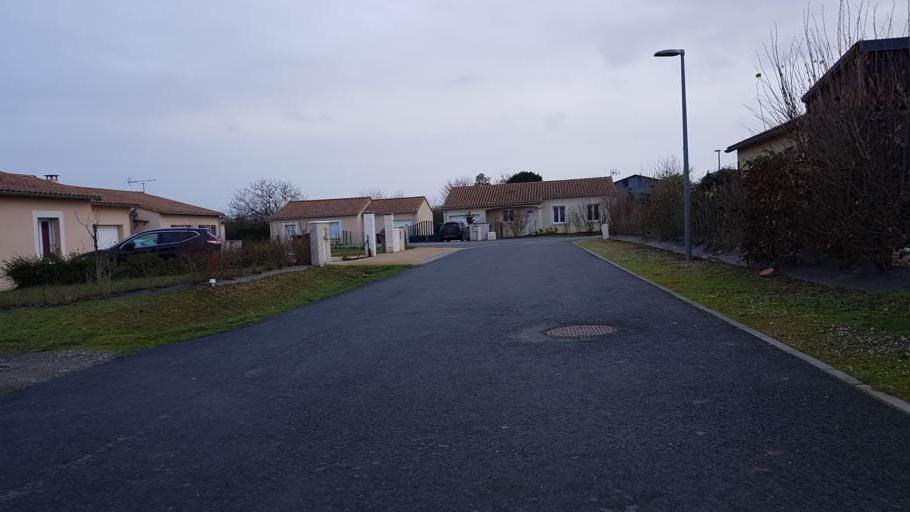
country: FR
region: Poitou-Charentes
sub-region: Departement de la Vienne
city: Avanton
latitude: 46.6625
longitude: 0.3100
